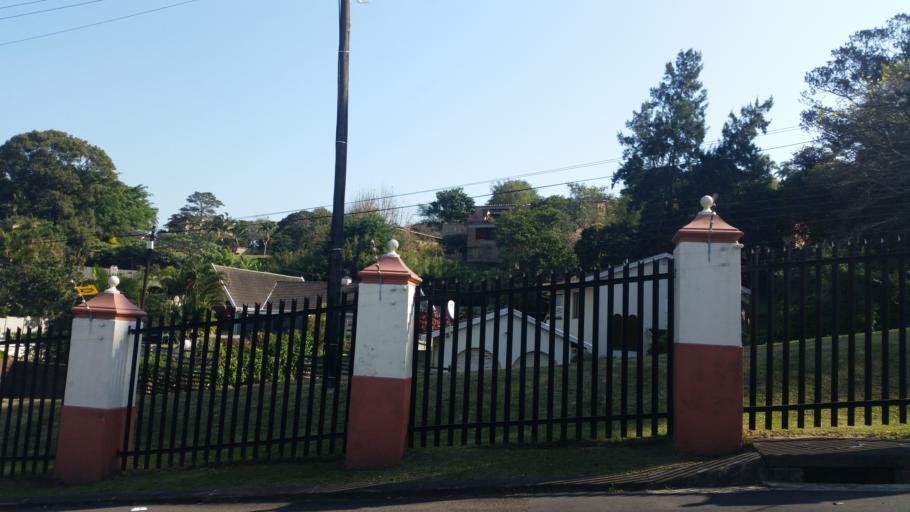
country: ZA
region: KwaZulu-Natal
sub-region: eThekwini Metropolitan Municipality
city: Berea
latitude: -29.8486
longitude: 30.9000
